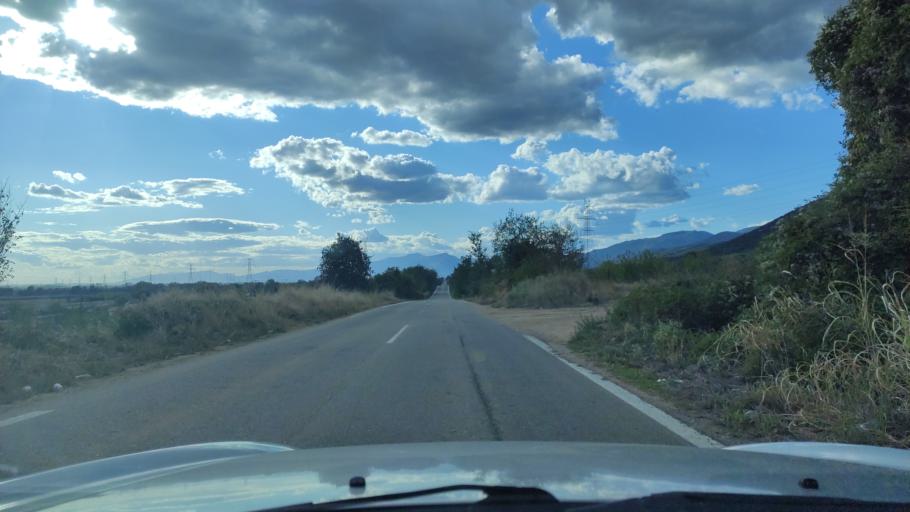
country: GR
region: East Macedonia and Thrace
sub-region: Nomos Rodopis
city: Iasmos
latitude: 41.1187
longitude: 25.1067
